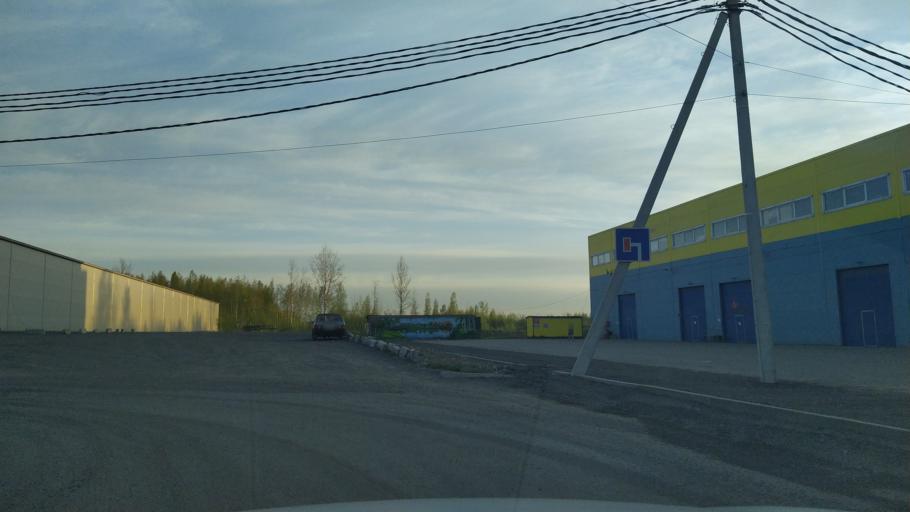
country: RU
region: St.-Petersburg
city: Obukhovo
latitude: 59.8063
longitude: 30.4593
